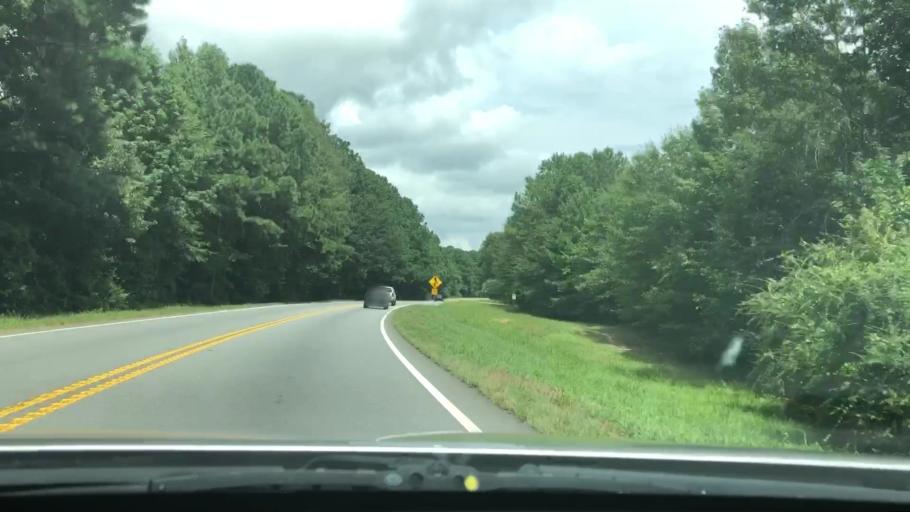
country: US
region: Georgia
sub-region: Lamar County
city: Barnesville
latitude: 33.1516
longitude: -84.1422
